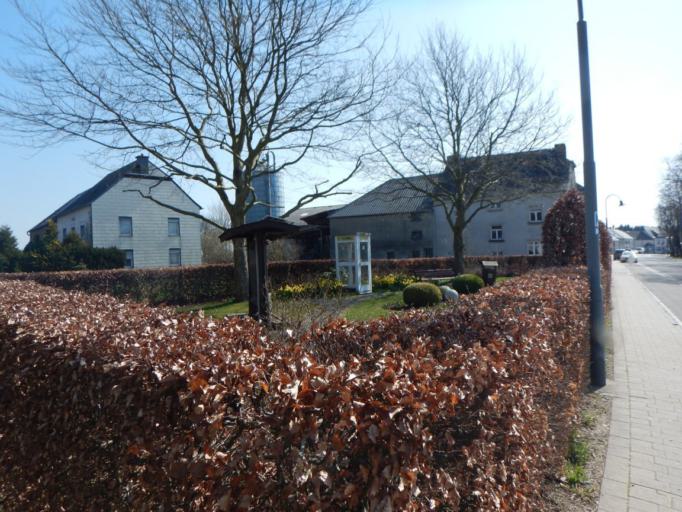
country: LU
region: Diekirch
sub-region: Canton de Diekirch
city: Bourscheid
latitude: 49.9459
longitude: 6.0805
